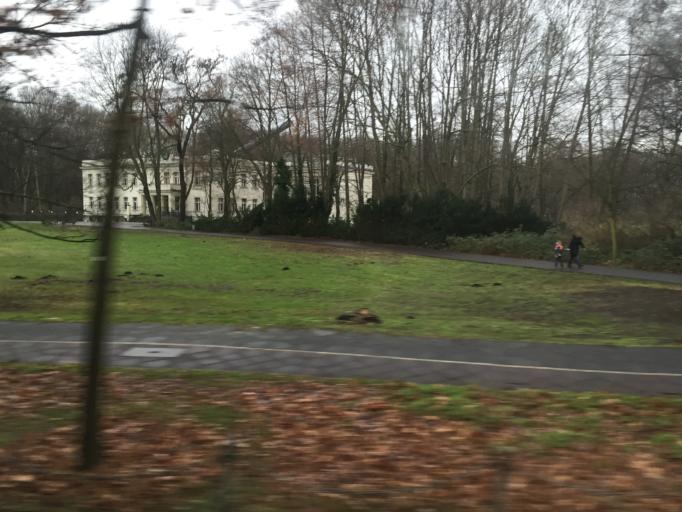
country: DE
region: Berlin
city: Plaenterwald
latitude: 52.4865
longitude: 13.4777
